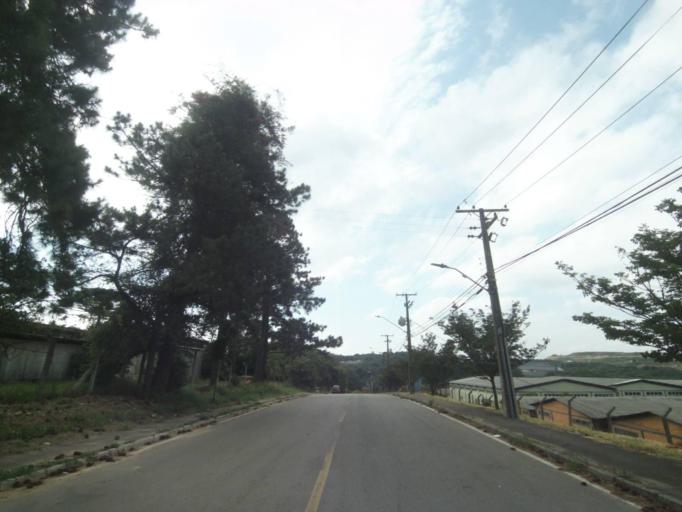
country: BR
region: Parana
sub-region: Araucaria
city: Araucaria
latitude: -25.5201
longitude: -49.3470
